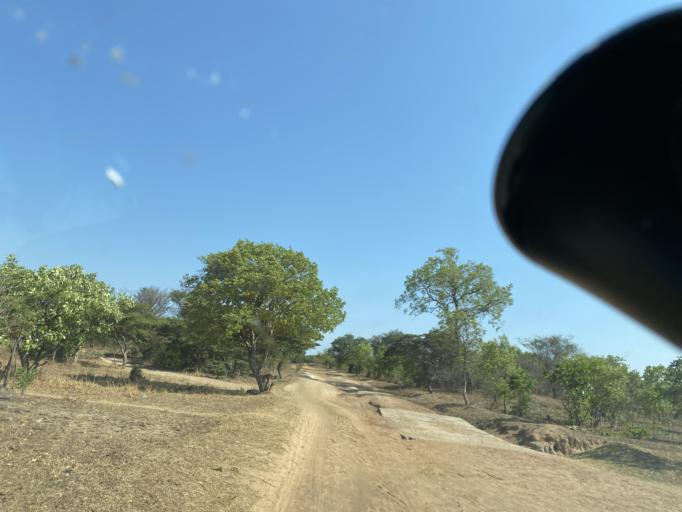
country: ZM
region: Lusaka
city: Chongwe
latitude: -15.2244
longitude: 28.8398
